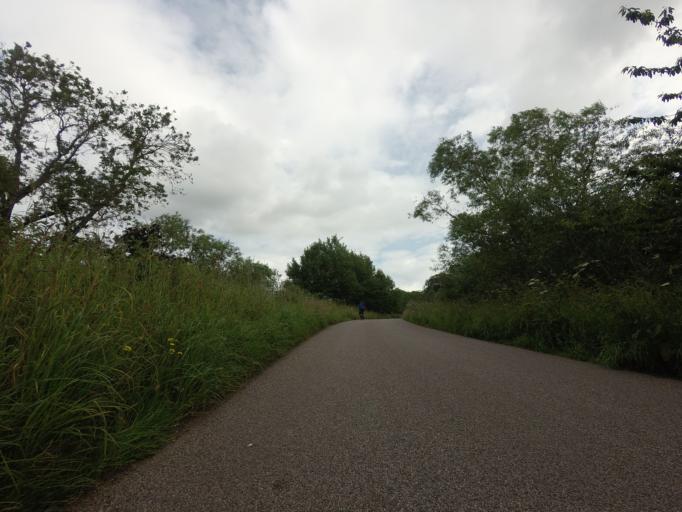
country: GB
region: Scotland
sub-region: Moray
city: Lhanbryd
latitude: 57.6515
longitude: -3.2383
